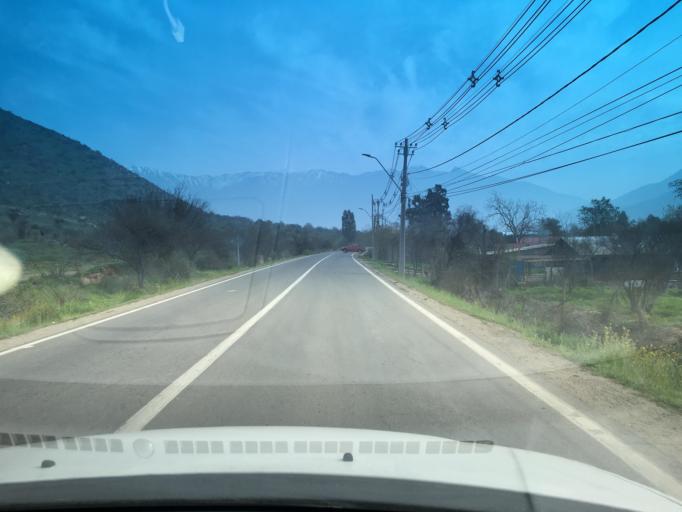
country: CL
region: Santiago Metropolitan
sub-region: Provincia de Chacabuco
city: Lampa
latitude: -33.2639
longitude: -70.8970
